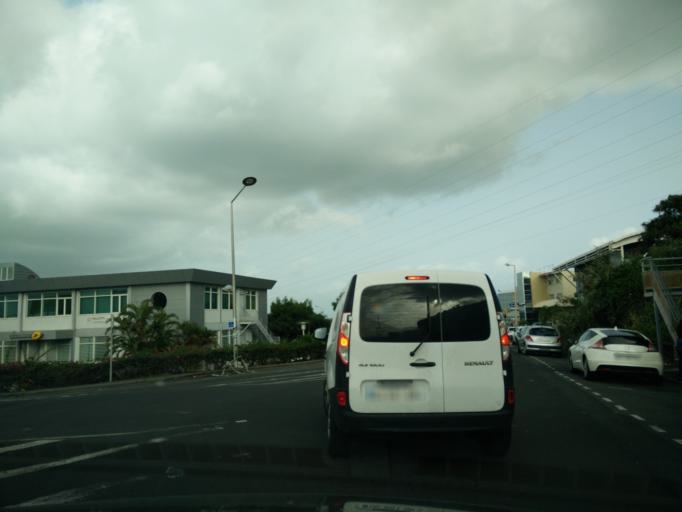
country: GP
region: Guadeloupe
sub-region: Guadeloupe
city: Baie-Mahault
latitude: 16.2380
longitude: -61.5710
